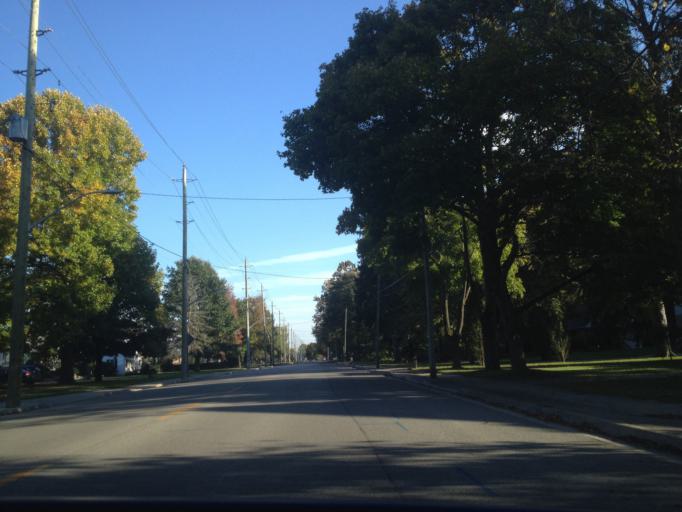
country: CA
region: Ontario
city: Delaware
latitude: 42.5996
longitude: -81.6011
